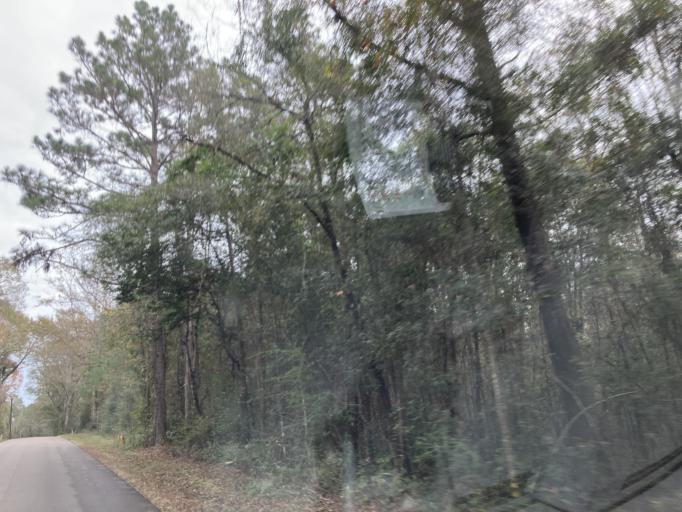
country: US
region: Mississippi
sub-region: Perry County
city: New Augusta
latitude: 31.0654
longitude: -89.1947
